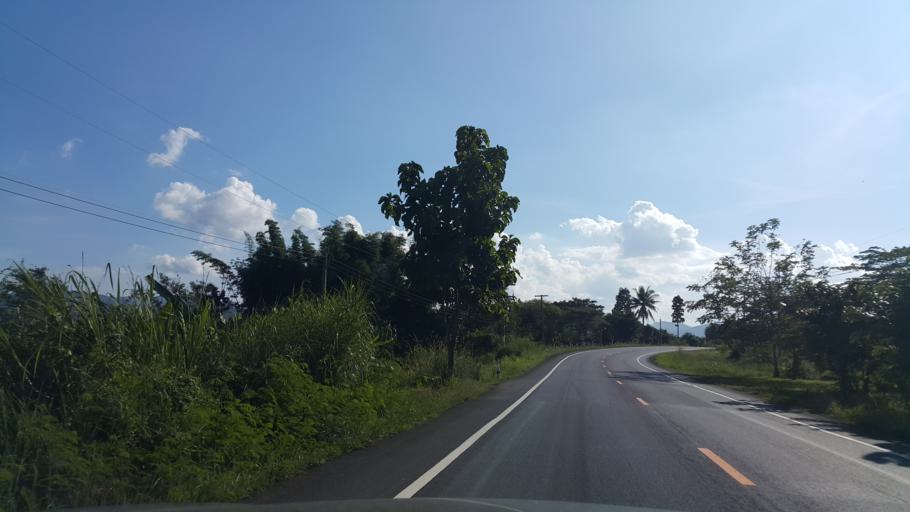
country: TH
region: Lamphun
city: Mae Tha
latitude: 18.4831
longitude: 99.1788
